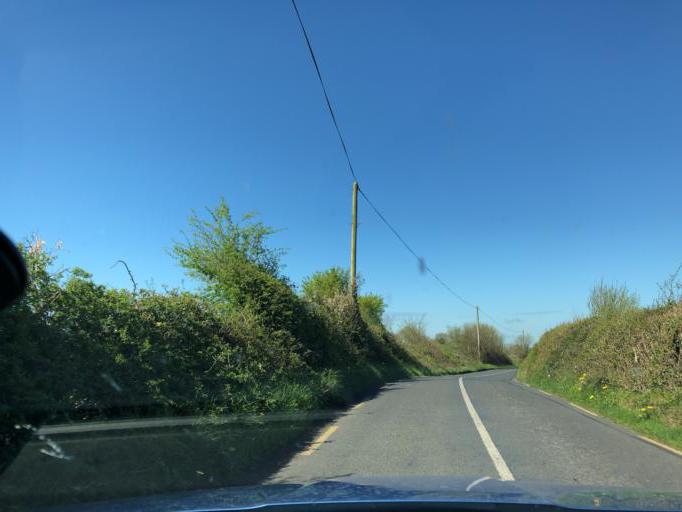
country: IE
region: Connaught
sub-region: County Galway
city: Portumna
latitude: 53.1622
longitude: -8.2401
